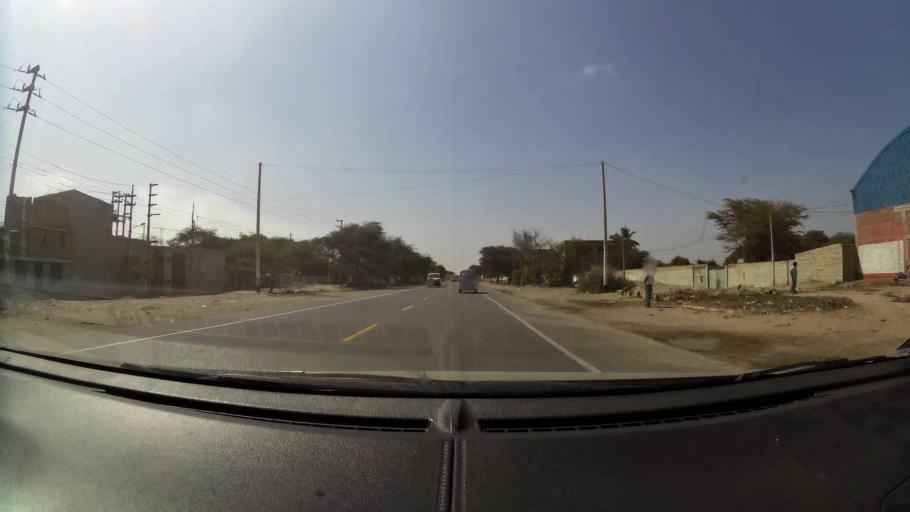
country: PE
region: Lambayeque
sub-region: Provincia de Chiclayo
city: Reque
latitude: -6.8250
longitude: -79.8294
